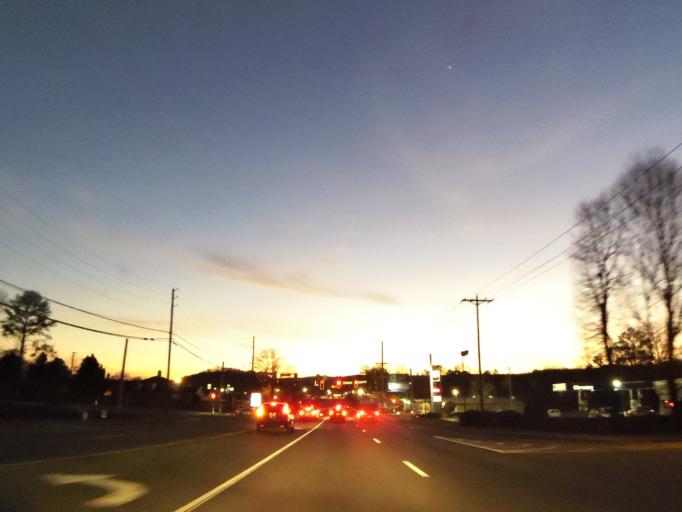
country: US
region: Georgia
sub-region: Whitfield County
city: Dalton
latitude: 34.8050
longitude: -84.9568
